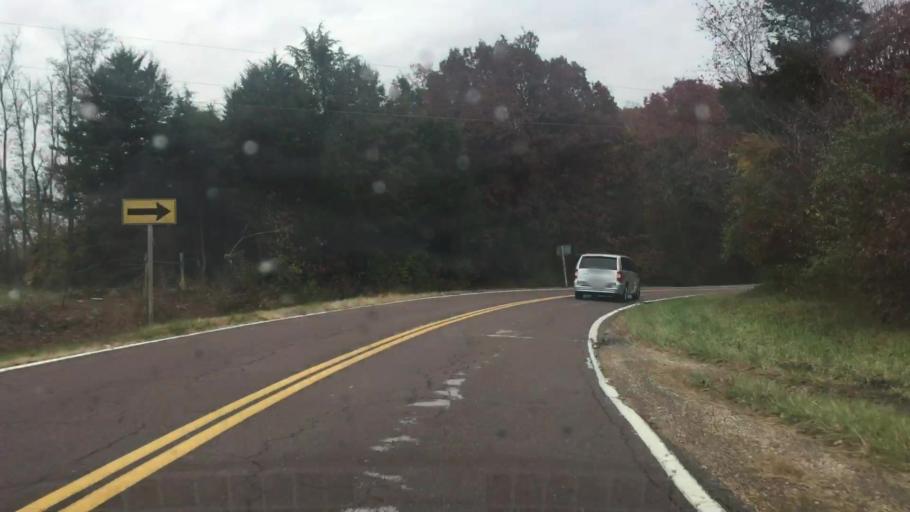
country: US
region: Missouri
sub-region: Callaway County
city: Fulton
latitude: 38.7885
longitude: -91.7604
